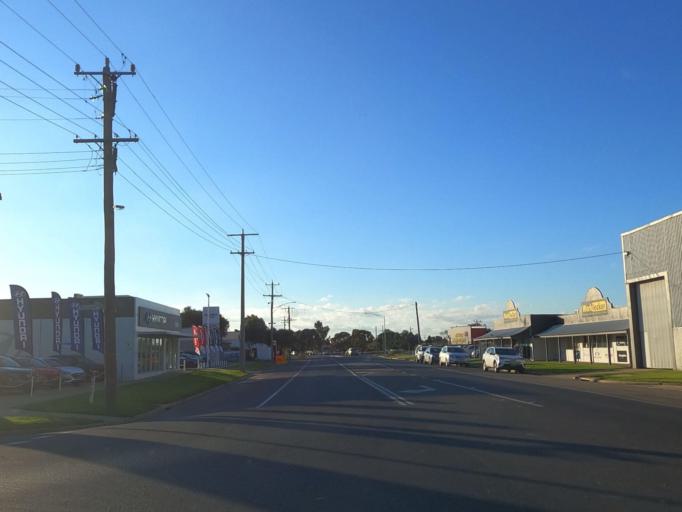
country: AU
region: Victoria
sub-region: Swan Hill
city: Swan Hill
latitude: -35.3362
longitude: 143.5602
